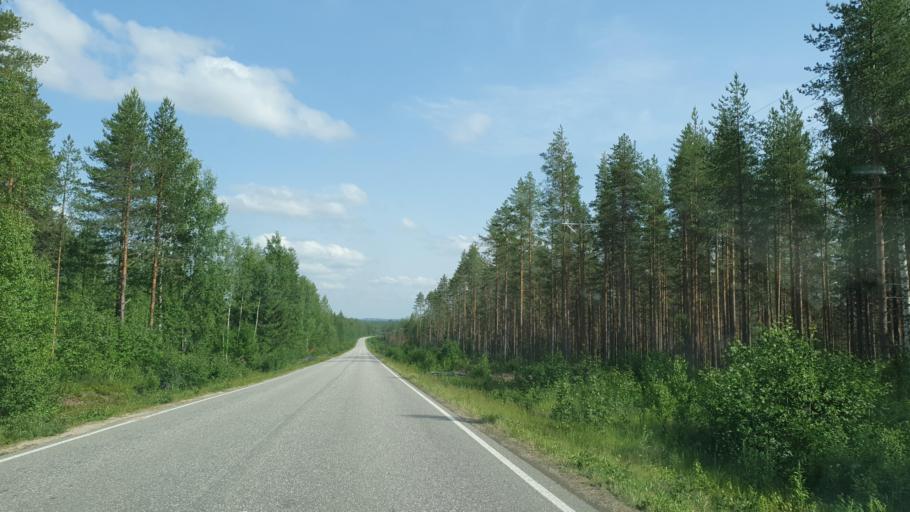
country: FI
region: Kainuu
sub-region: Kehys-Kainuu
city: Kuhmo
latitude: 64.0990
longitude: 29.7726
